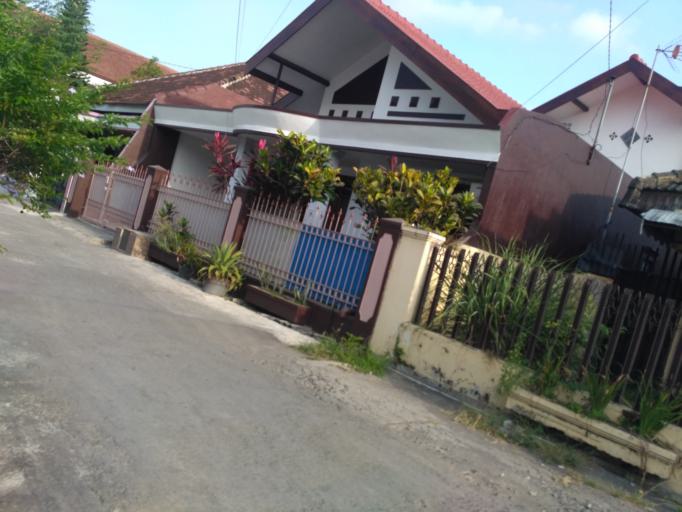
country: ID
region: East Java
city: Malang
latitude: -7.9379
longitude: 112.6320
